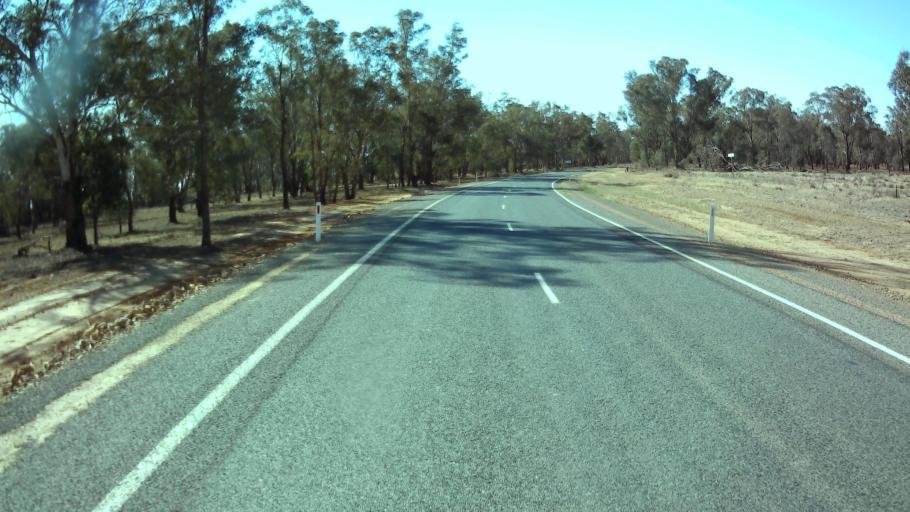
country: AU
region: New South Wales
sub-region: Weddin
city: Grenfell
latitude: -33.7209
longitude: 148.0815
